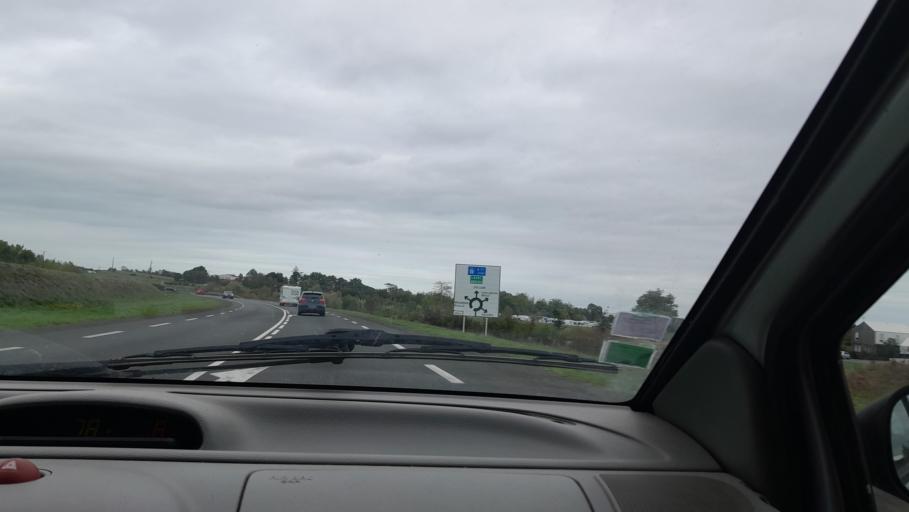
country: FR
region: Pays de la Loire
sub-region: Departement de la Loire-Atlantique
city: Saint-Gereon
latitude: 47.3841
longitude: -1.2028
